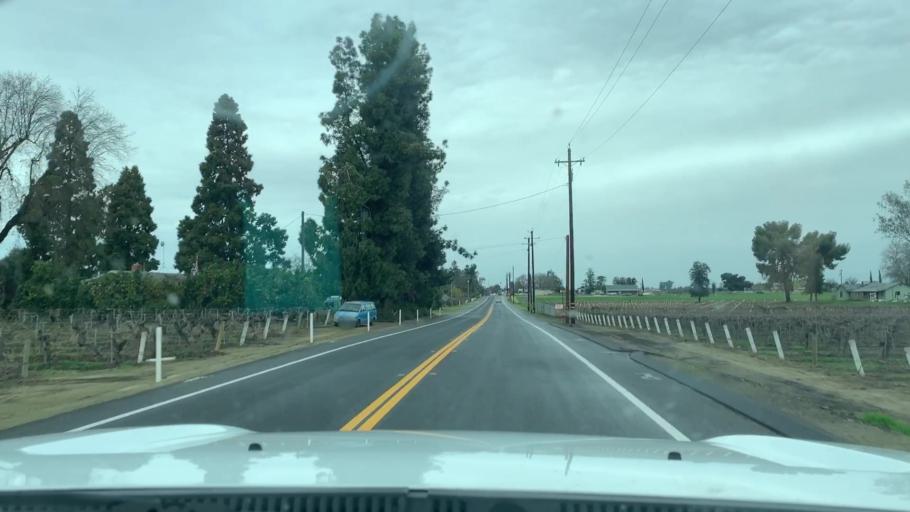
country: US
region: California
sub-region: Fresno County
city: Fowler
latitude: 36.5716
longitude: -119.6825
